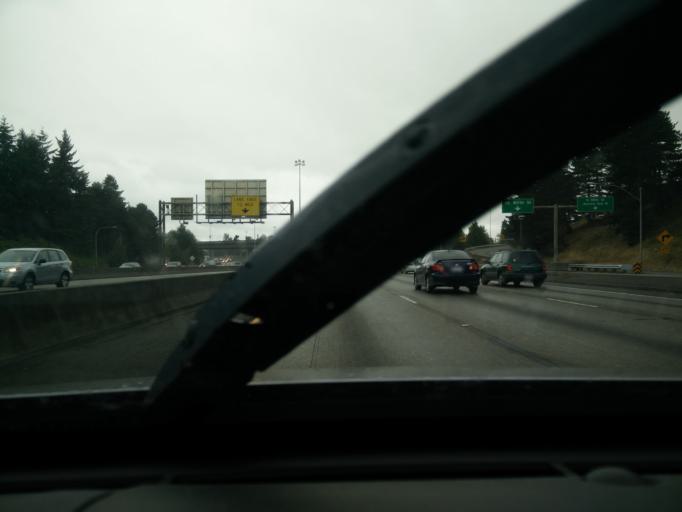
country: US
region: Washington
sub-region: King County
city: Shoreline
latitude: 47.6923
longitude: -122.3294
